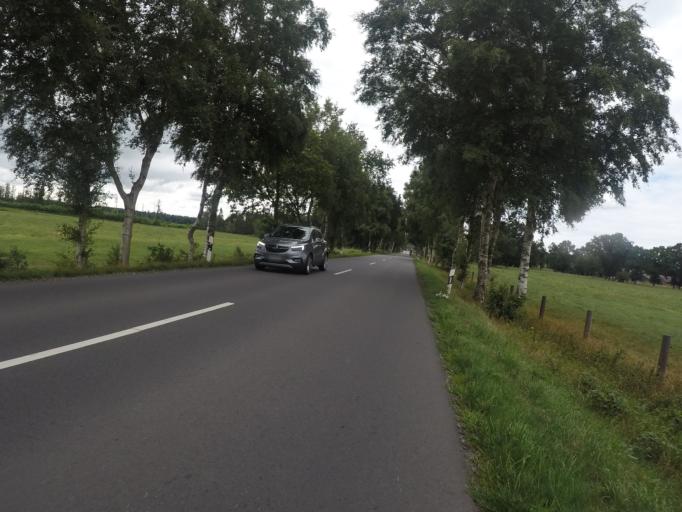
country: DE
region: Lower Saxony
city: Wingst
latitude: 53.7074
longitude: 9.0704
